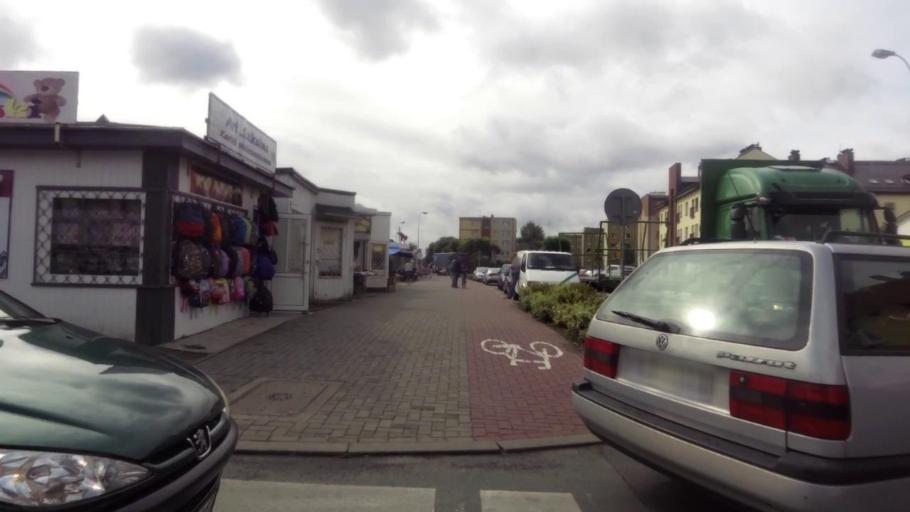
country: PL
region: West Pomeranian Voivodeship
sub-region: Powiat mysliborski
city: Debno
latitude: 52.7376
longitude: 14.6966
